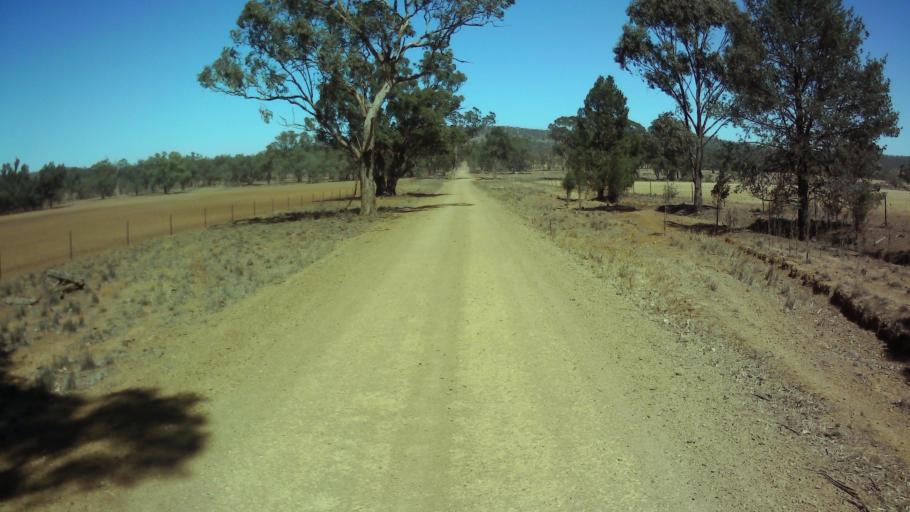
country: AU
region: New South Wales
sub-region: Weddin
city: Grenfell
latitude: -33.7059
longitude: 147.9853
